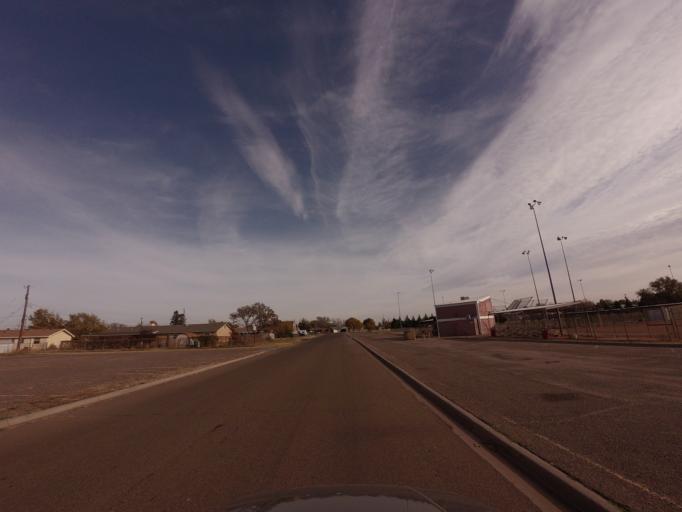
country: US
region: New Mexico
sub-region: Curry County
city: Clovis
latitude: 34.4257
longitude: -103.2275
